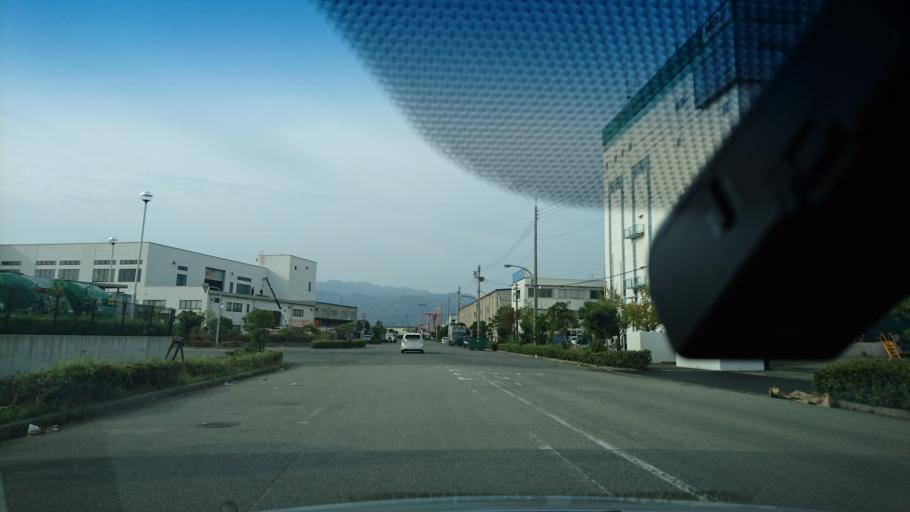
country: JP
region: Hyogo
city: Ashiya
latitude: 34.6932
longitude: 135.2863
